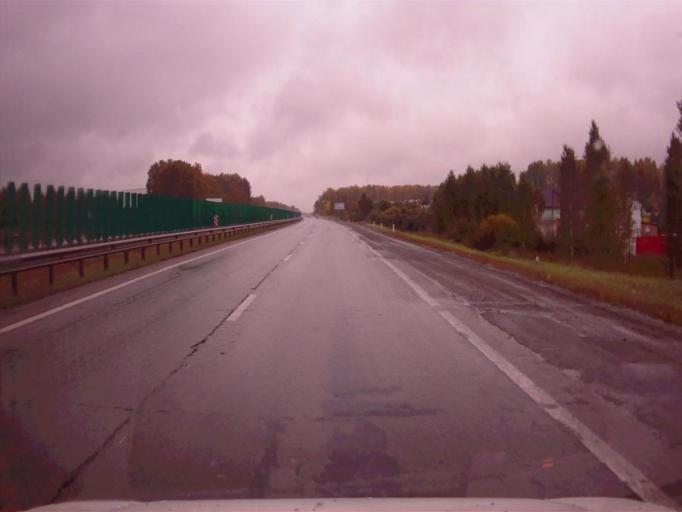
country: RU
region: Chelyabinsk
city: Dolgoderevenskoye
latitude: 55.3284
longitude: 61.3246
